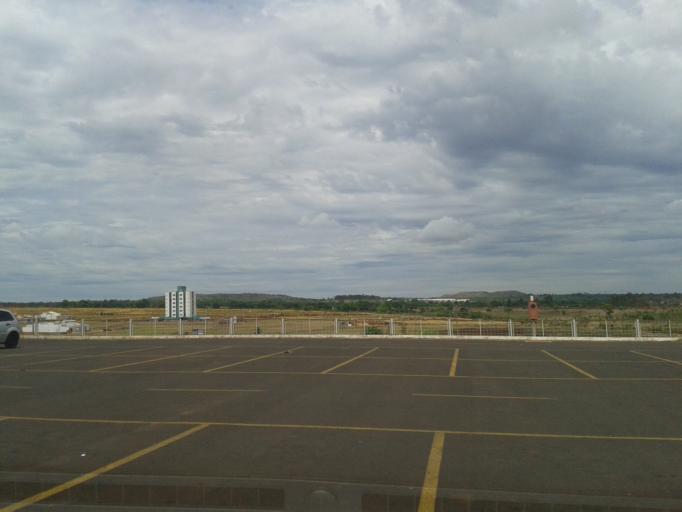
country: BR
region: Minas Gerais
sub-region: Ituiutaba
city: Ituiutaba
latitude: -18.9948
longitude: -49.4680
